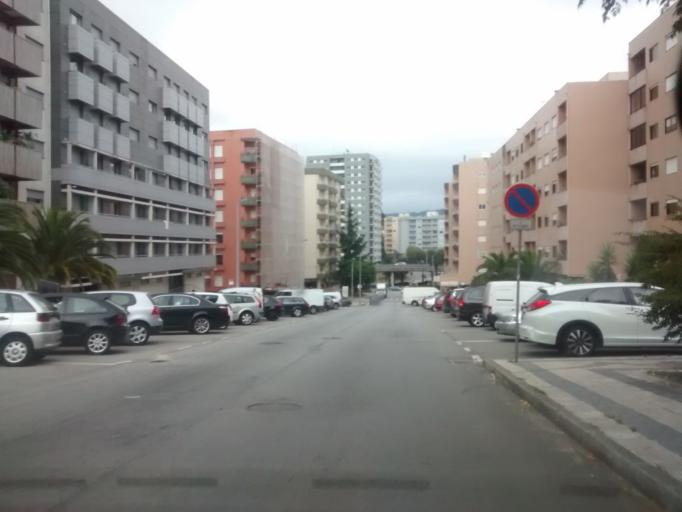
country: PT
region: Braga
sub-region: Braga
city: Braga
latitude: 41.5597
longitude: -8.4101
